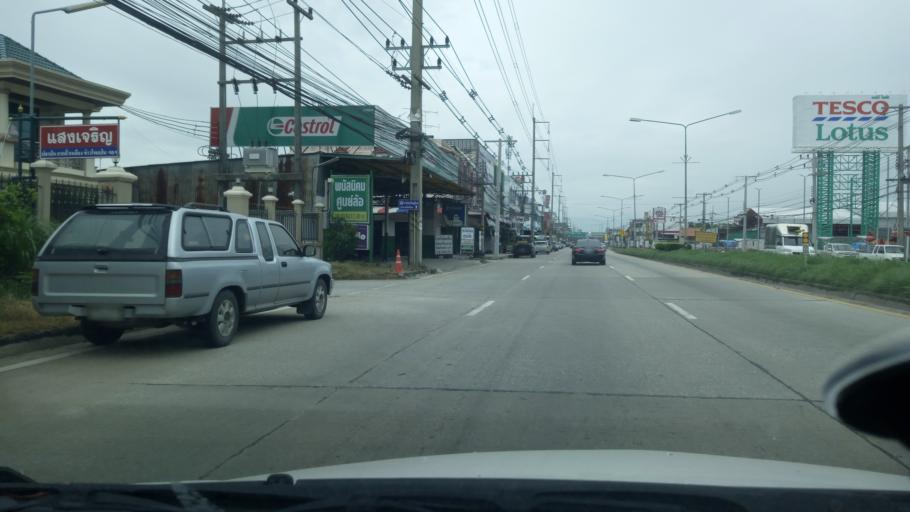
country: TH
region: Chon Buri
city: Phanat Nikhom
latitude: 13.4469
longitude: 101.1681
